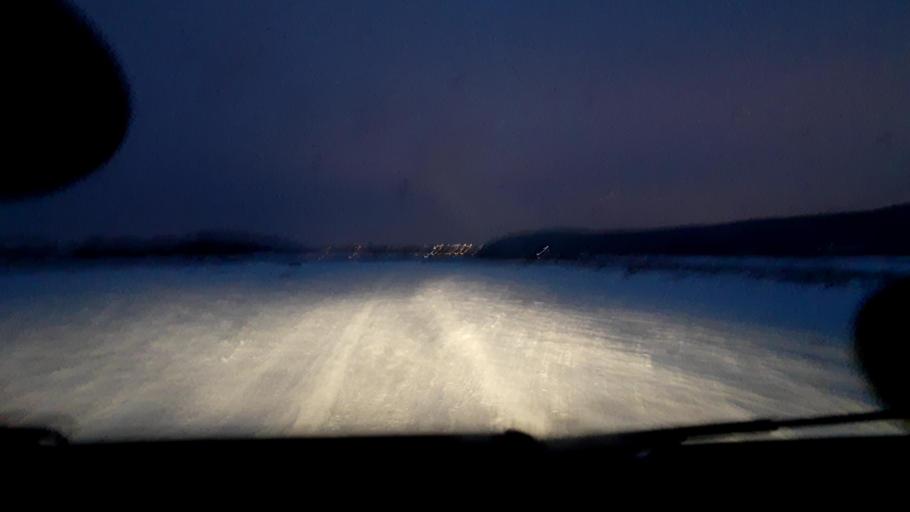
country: RU
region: Bashkortostan
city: Ufa
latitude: 54.8268
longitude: 56.1643
